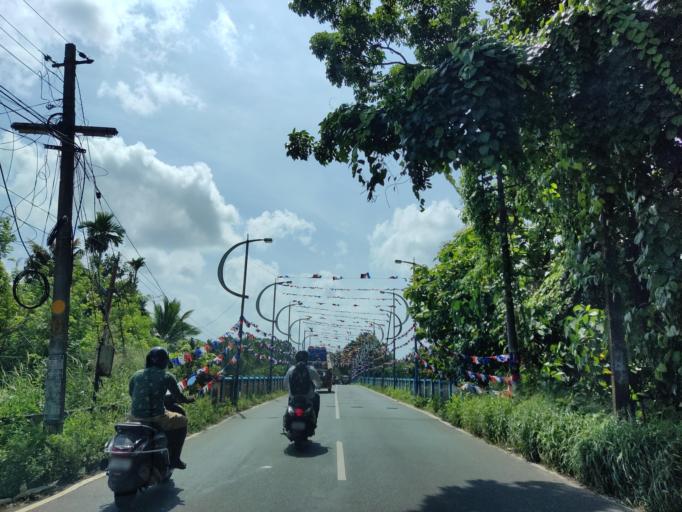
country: IN
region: Kerala
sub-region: Alappuzha
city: Mavelikara
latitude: 9.2626
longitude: 76.5429
